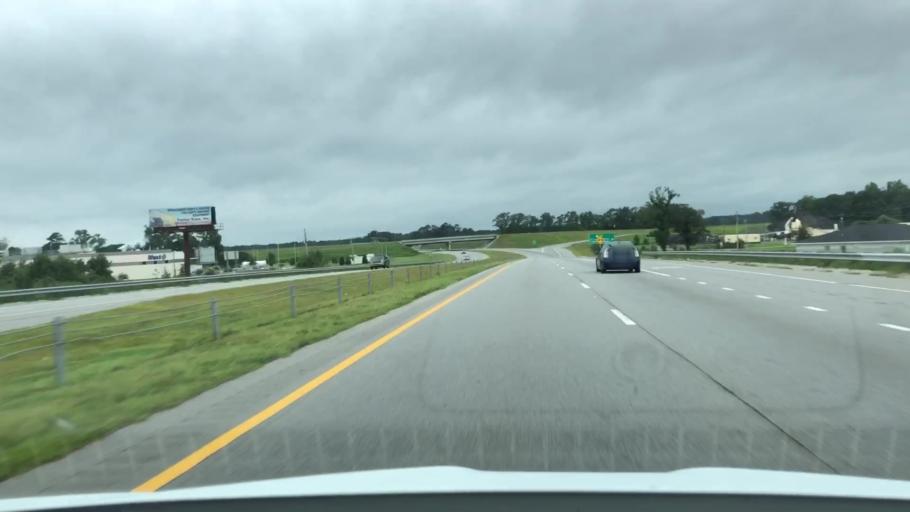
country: US
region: North Carolina
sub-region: Lenoir County
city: Kinston
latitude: 35.2629
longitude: -77.6683
